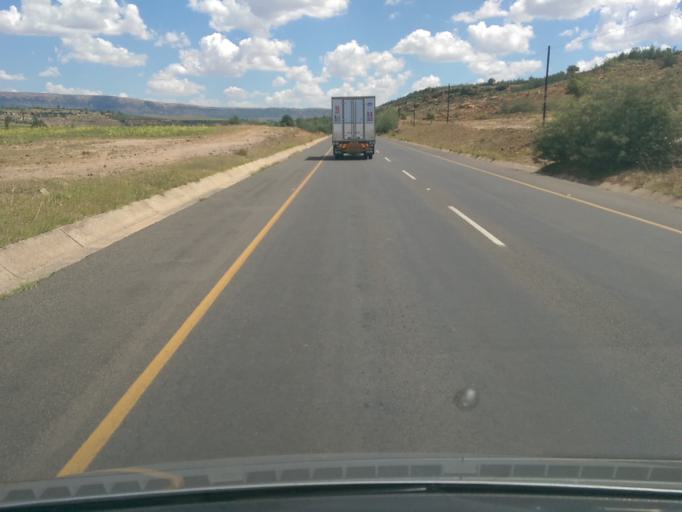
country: LS
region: Maseru
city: Maseru
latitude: -29.3939
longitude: 27.5415
